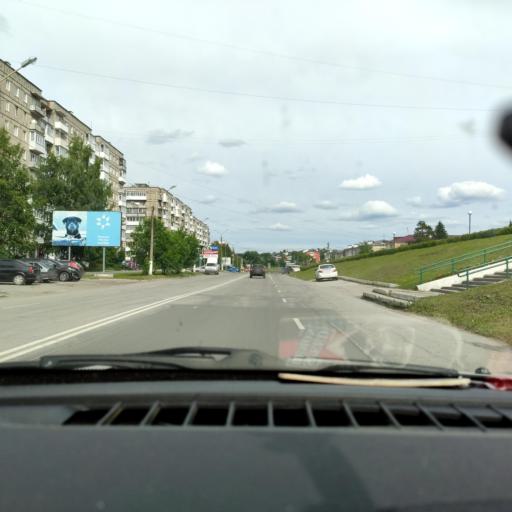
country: RU
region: Perm
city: Chusovoy
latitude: 58.2717
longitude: 57.8056
